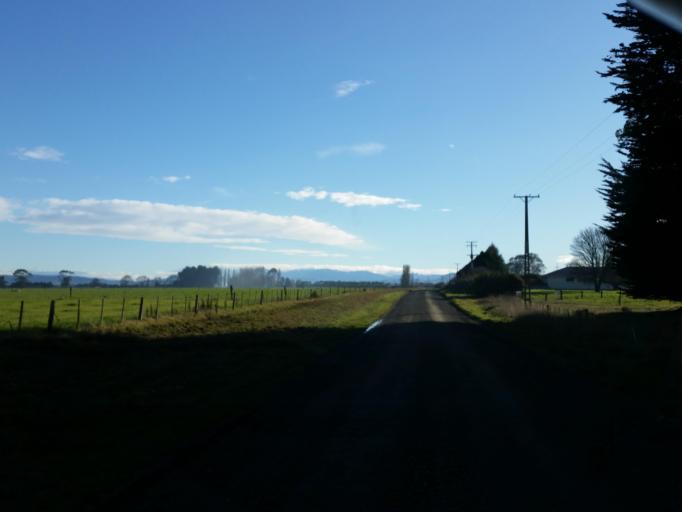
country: NZ
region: Southland
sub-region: Southland District
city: Winton
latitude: -46.1323
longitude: 168.1065
